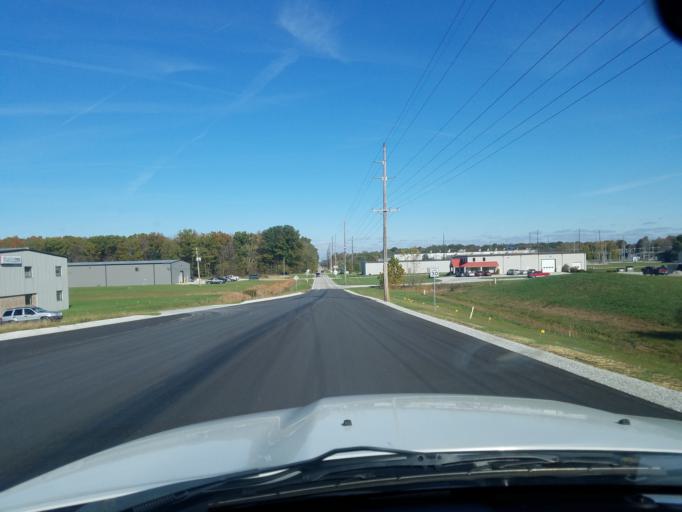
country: US
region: Indiana
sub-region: Jennings County
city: North Vernon
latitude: 39.0337
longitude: -85.6260
